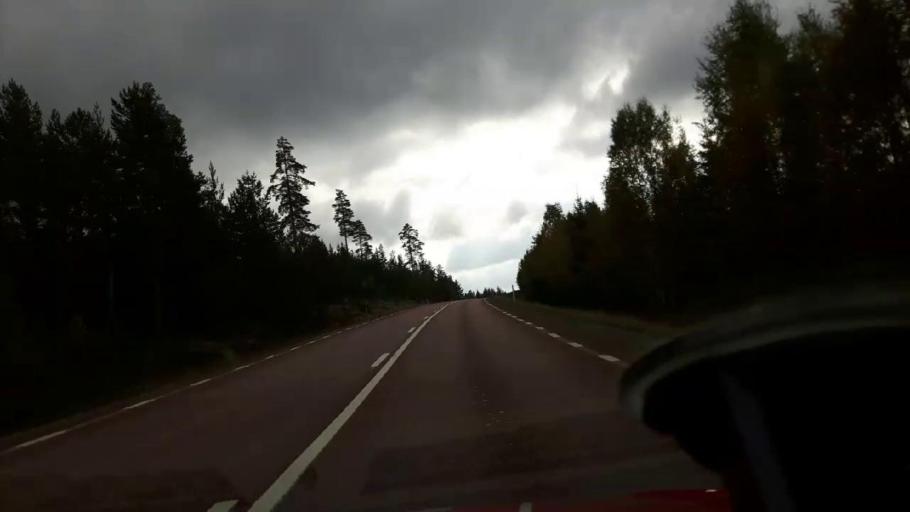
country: SE
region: Gaevleborg
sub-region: Soderhamns Kommun
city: Ljusne
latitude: 61.1207
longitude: 16.9350
